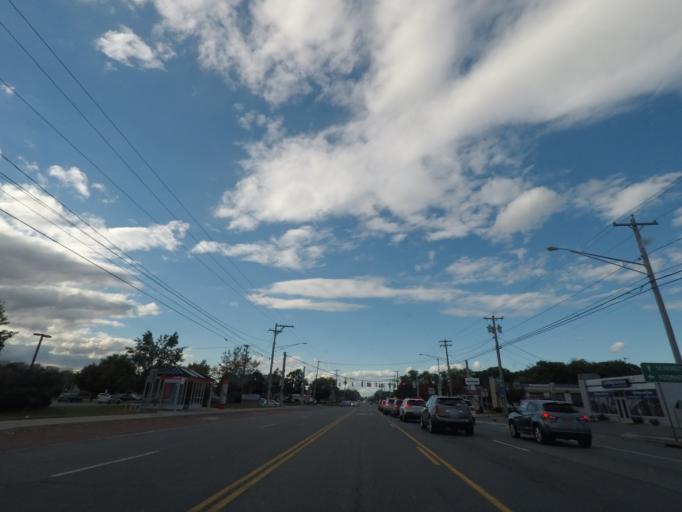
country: US
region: New York
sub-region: Albany County
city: Colonie
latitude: 42.7319
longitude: -73.8491
